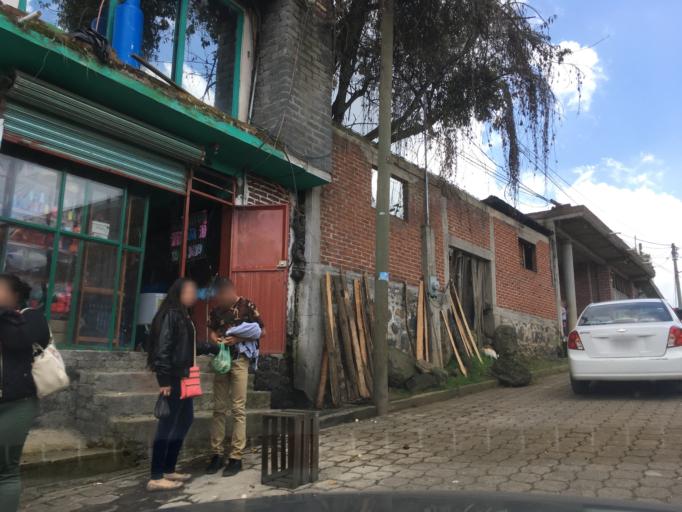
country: MX
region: Michoacan
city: Capacuaro
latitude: 19.5929
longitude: -102.0017
